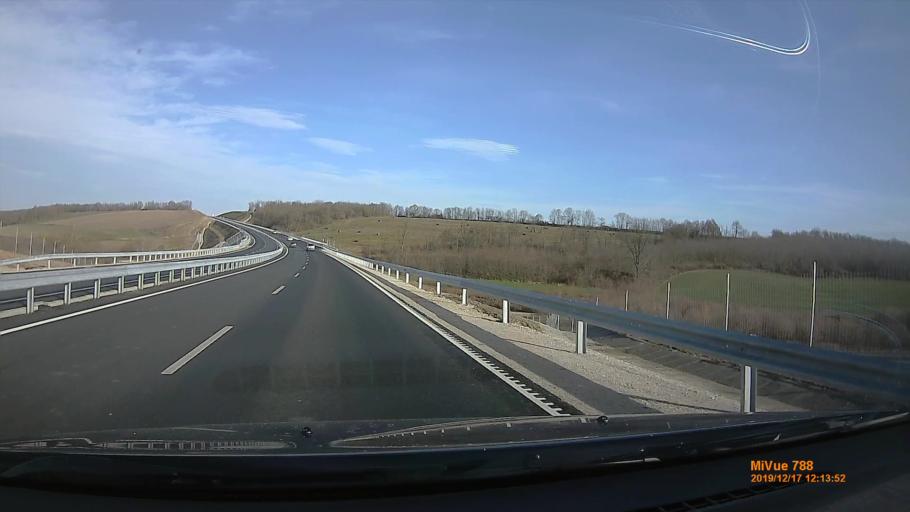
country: HU
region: Somogy
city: Kaposvar
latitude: 46.4578
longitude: 17.7851
